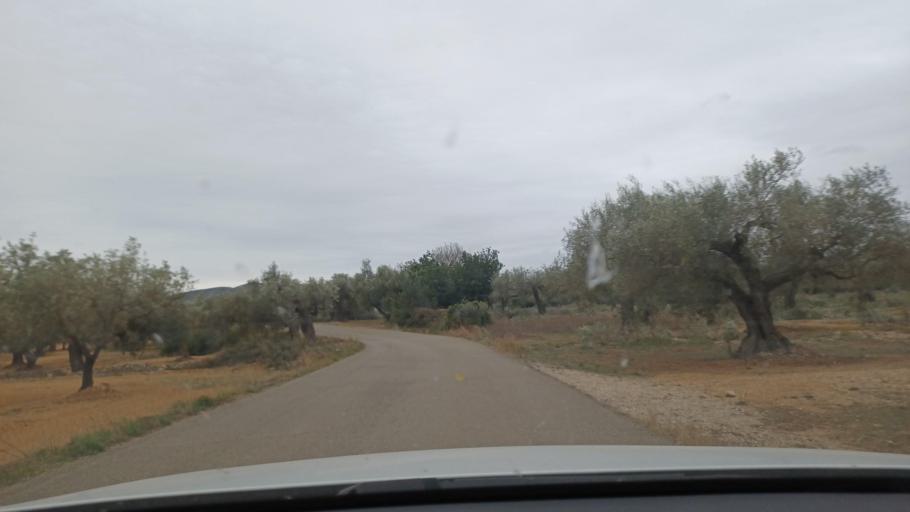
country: ES
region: Valencia
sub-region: Provincia de Castello
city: Canet lo Roig
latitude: 40.5808
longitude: 0.2820
